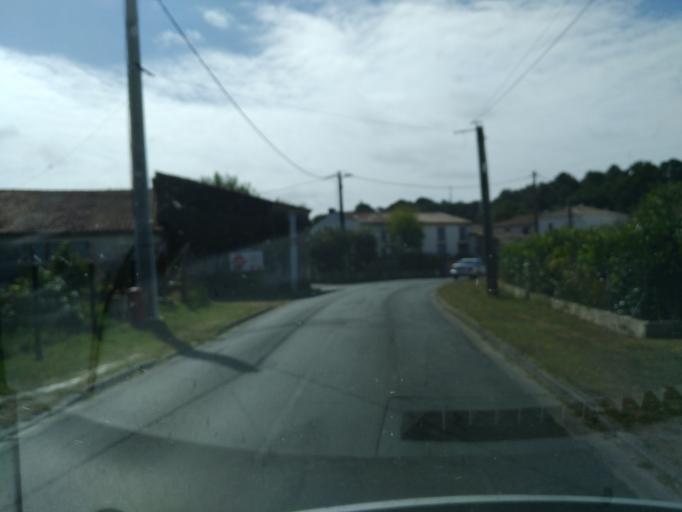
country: FR
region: Poitou-Charentes
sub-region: Departement de la Charente-Maritime
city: Saint-Palais-sur-Mer
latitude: 45.6710
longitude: -1.0846
